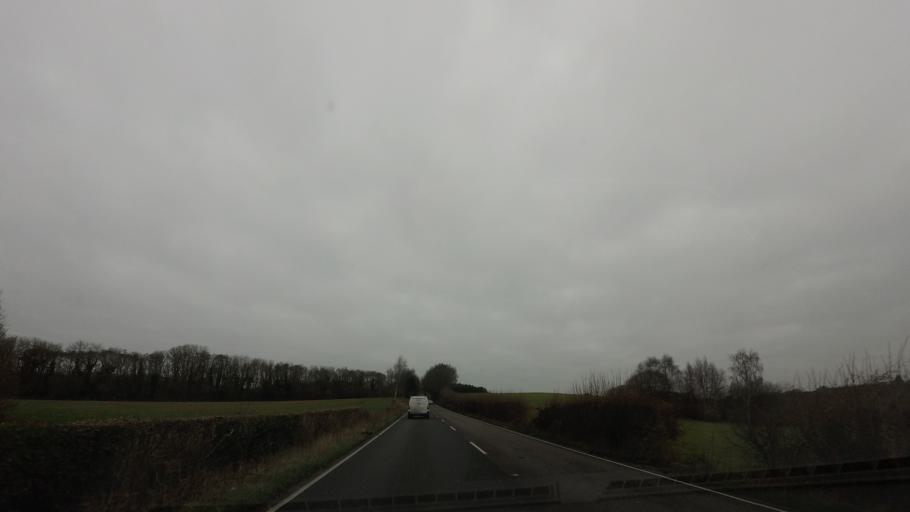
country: GB
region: England
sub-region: East Sussex
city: Battle
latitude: 50.9326
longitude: 0.5225
